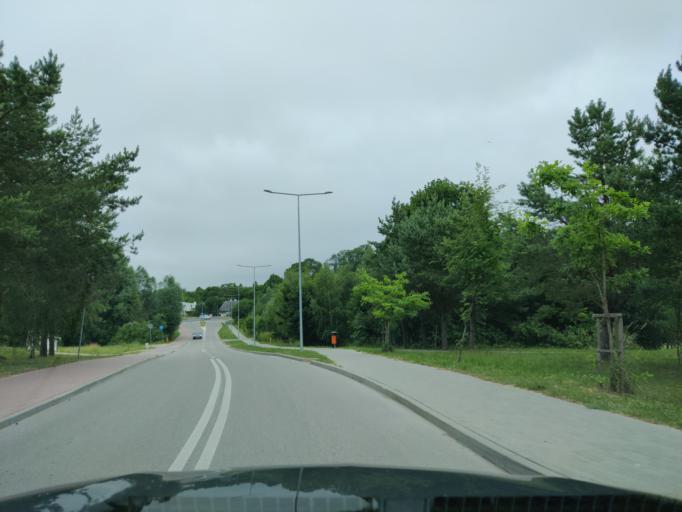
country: PL
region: Warmian-Masurian Voivodeship
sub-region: Powiat gizycki
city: Ryn
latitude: 53.9362
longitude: 21.5392
